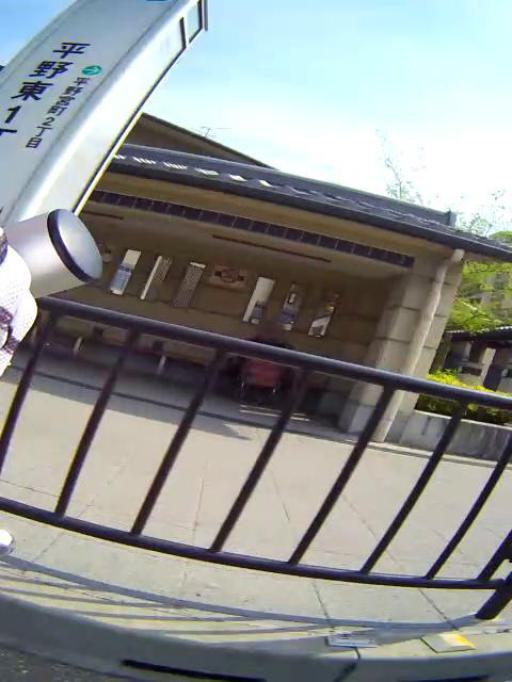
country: JP
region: Osaka
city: Yao
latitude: 34.6248
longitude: 135.5591
